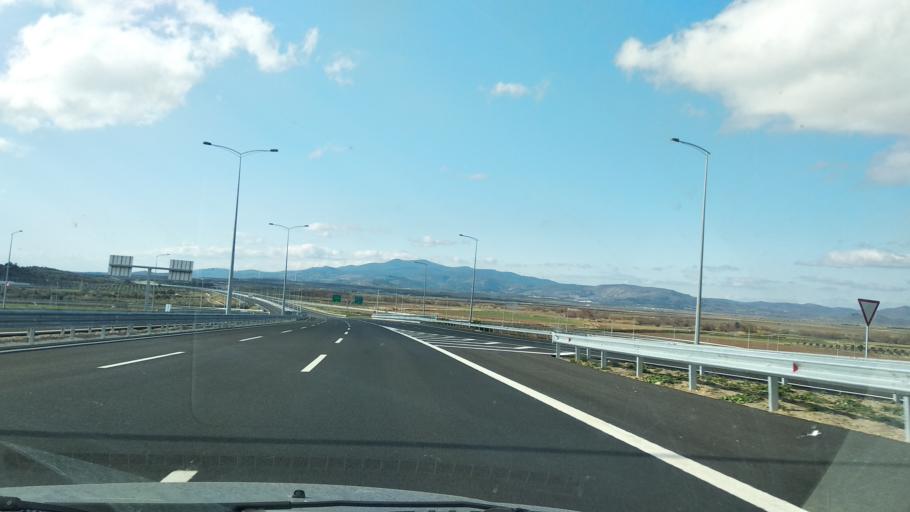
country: TR
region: Izmir
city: Zeytindag
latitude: 38.9735
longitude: 27.0468
